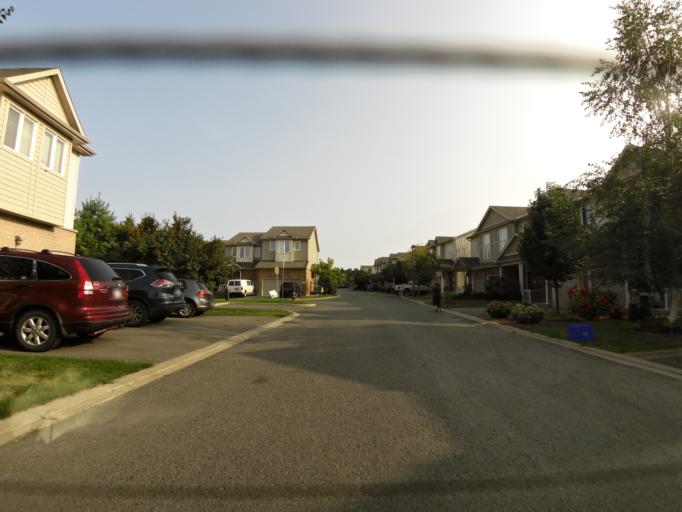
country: CA
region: Ontario
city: Clarence-Rockland
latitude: 45.4922
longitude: -75.4924
